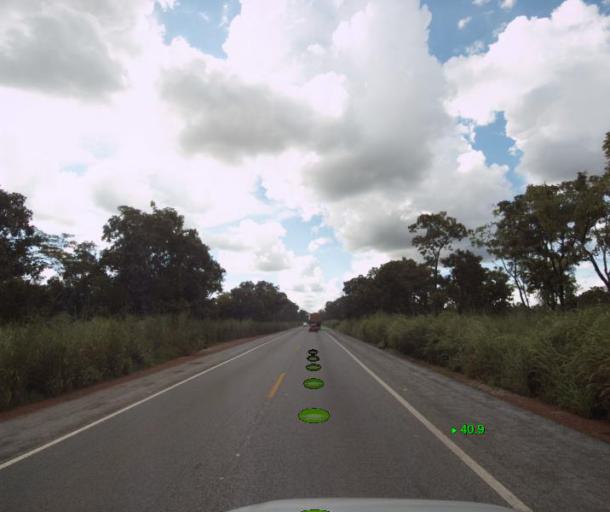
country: BR
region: Goias
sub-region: Porangatu
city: Porangatu
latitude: -13.1784
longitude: -49.1692
